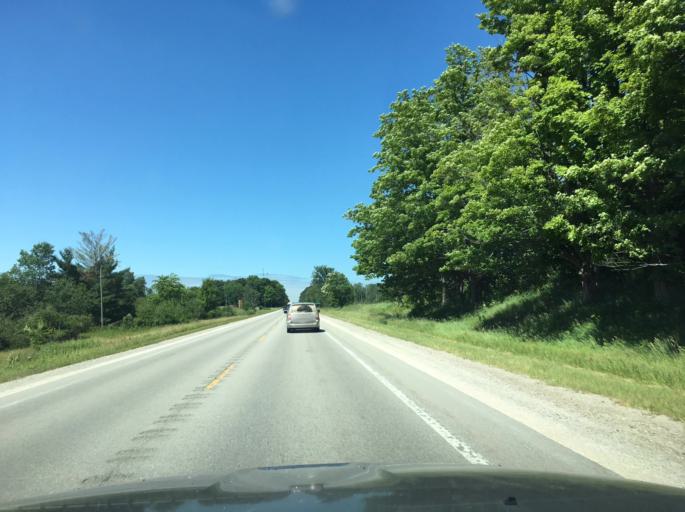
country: US
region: Michigan
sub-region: Osceola County
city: Reed City
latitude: 43.8877
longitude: -85.5762
